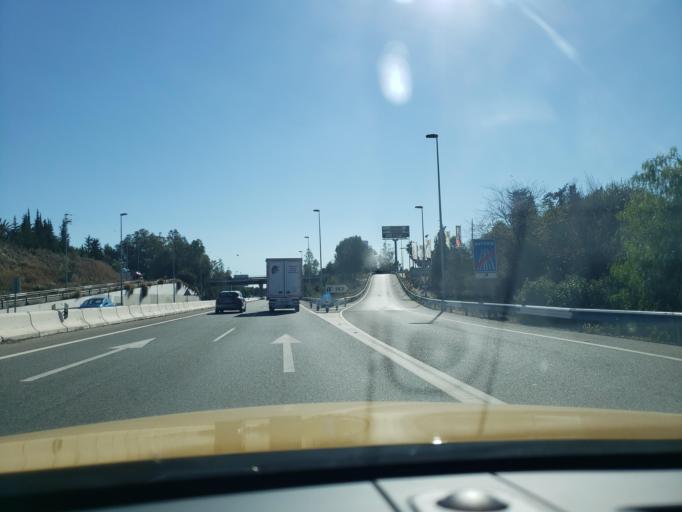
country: ES
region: Andalusia
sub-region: Provincia de Malaga
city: Marbella
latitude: 36.5151
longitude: -4.8648
